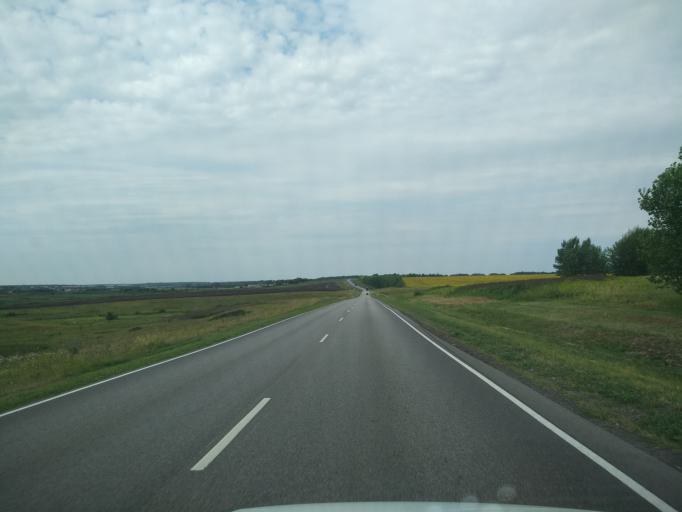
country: RU
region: Voronezj
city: Pereleshinskiy
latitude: 51.8589
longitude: 40.3486
